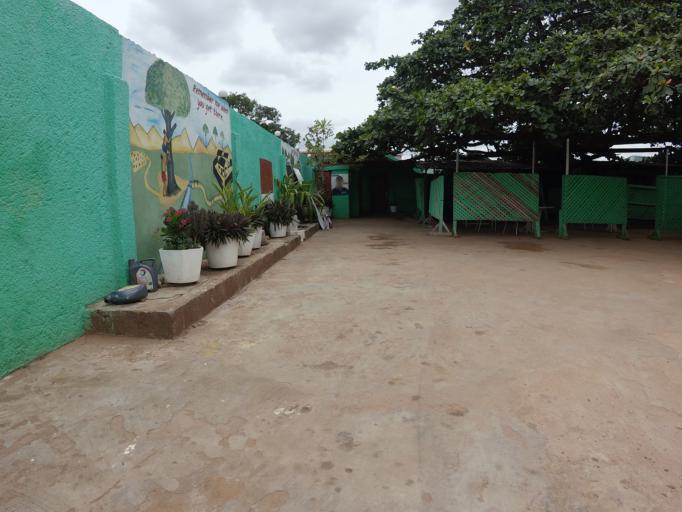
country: GH
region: Greater Accra
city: Dome
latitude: 5.6062
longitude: -0.2243
